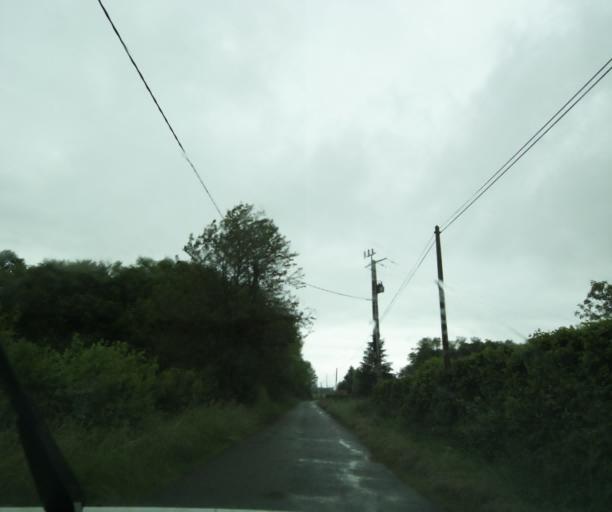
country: FR
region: Bourgogne
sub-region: Departement de Saone-et-Loire
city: Ciry-le-Noble
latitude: 46.5307
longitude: 4.3029
